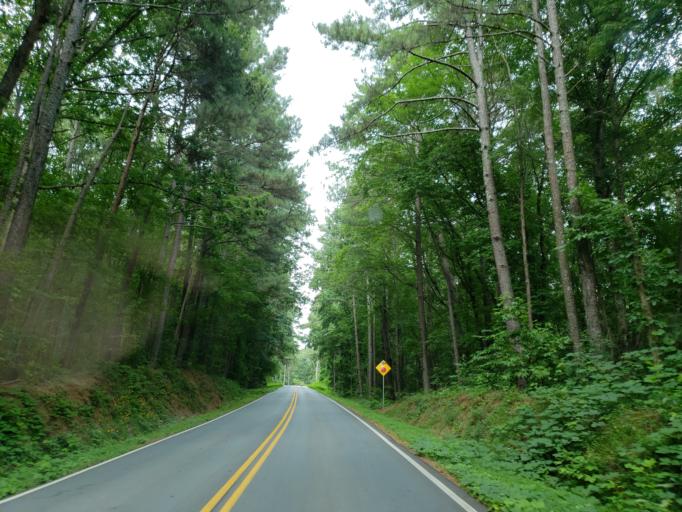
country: US
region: Georgia
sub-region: Pickens County
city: Jasper
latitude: 34.4451
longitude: -84.4041
